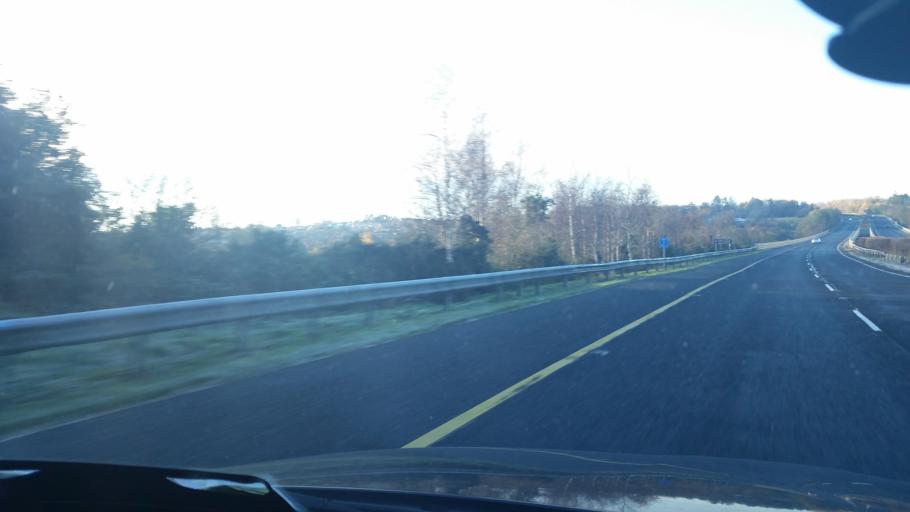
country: IE
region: Leinster
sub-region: Wicklow
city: Arklow
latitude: 52.8092
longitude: -6.1696
